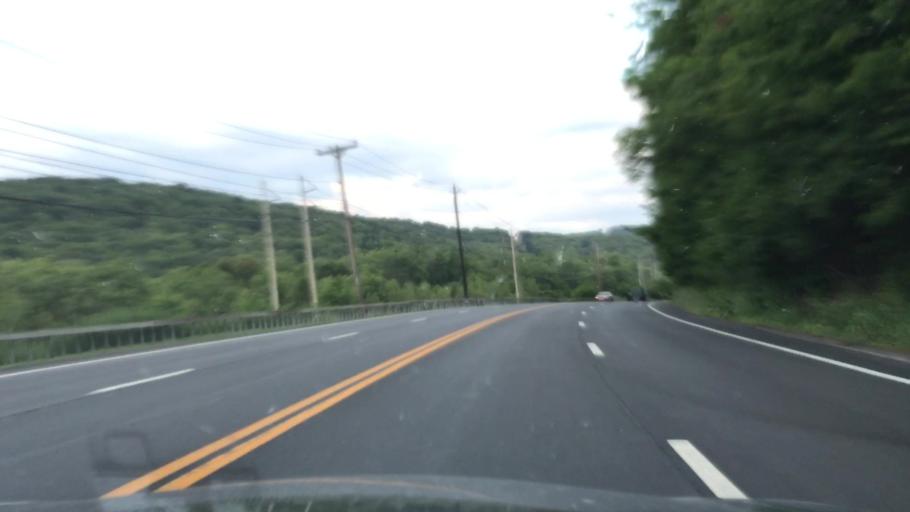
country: US
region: New York
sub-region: Rockland County
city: Sloatsburg
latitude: 41.2185
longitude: -74.1859
